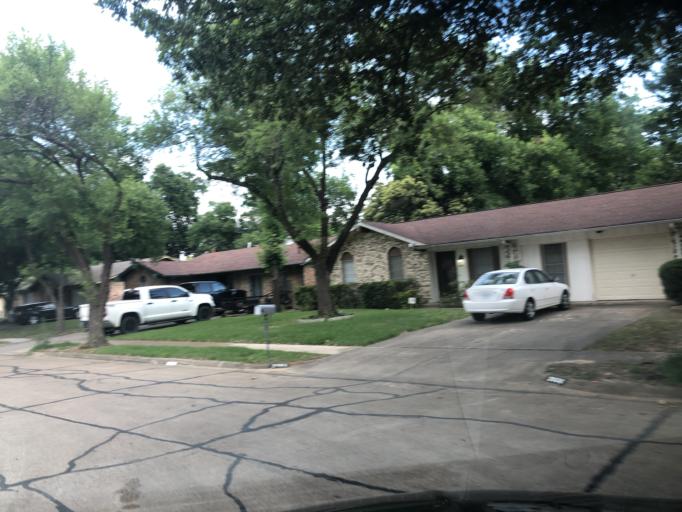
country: US
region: Texas
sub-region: Dallas County
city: Irving
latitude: 32.7900
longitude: -96.9717
